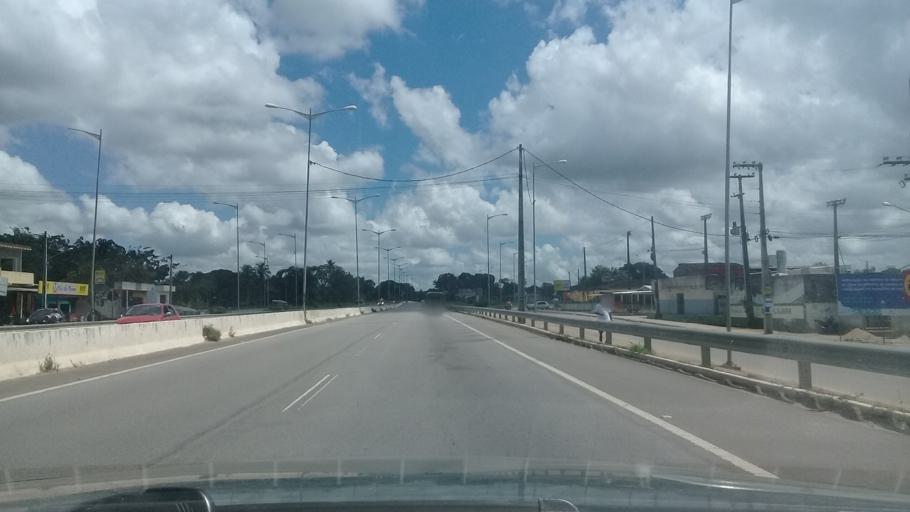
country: BR
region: Pernambuco
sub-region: Sao Lourenco Da Mata
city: Sao Lourenco da Mata
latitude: -7.9422
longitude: -35.1224
